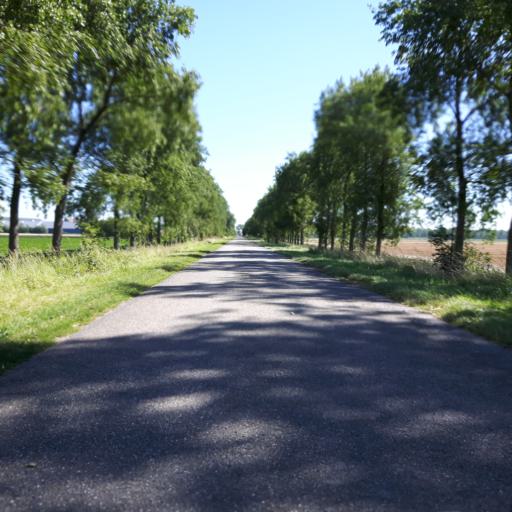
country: NL
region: Zeeland
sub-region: Gemeente Noord-Beveland
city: Kamperland
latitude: 51.5731
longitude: 3.7939
